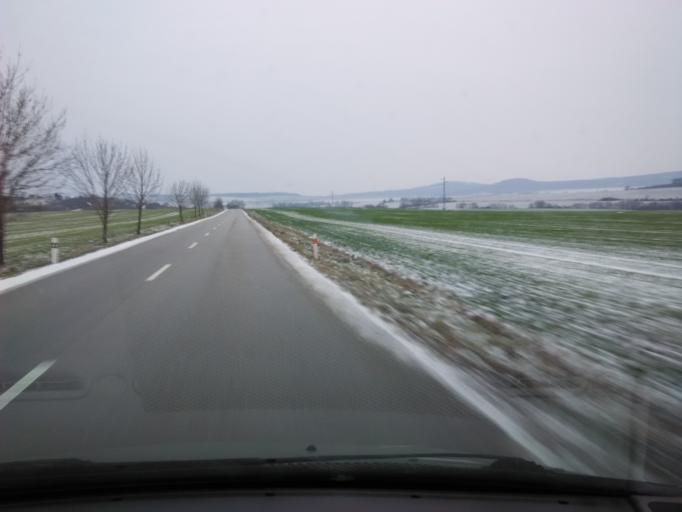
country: SK
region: Nitriansky
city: Tlmace
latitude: 48.3334
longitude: 18.4929
